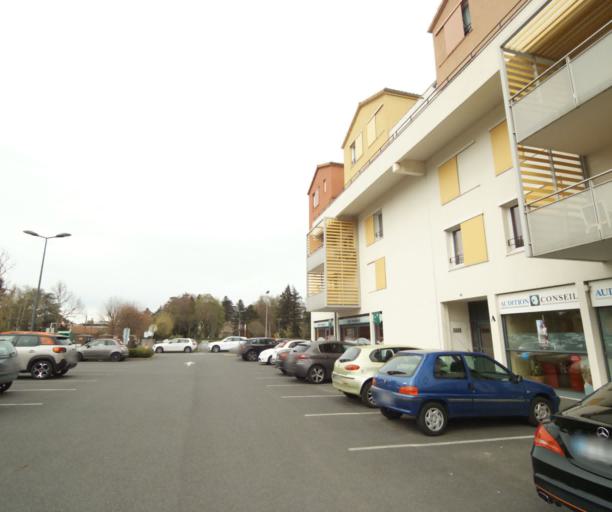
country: FR
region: Bourgogne
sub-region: Departement de Saone-et-Loire
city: Macon
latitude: 46.3094
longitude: 4.8123
